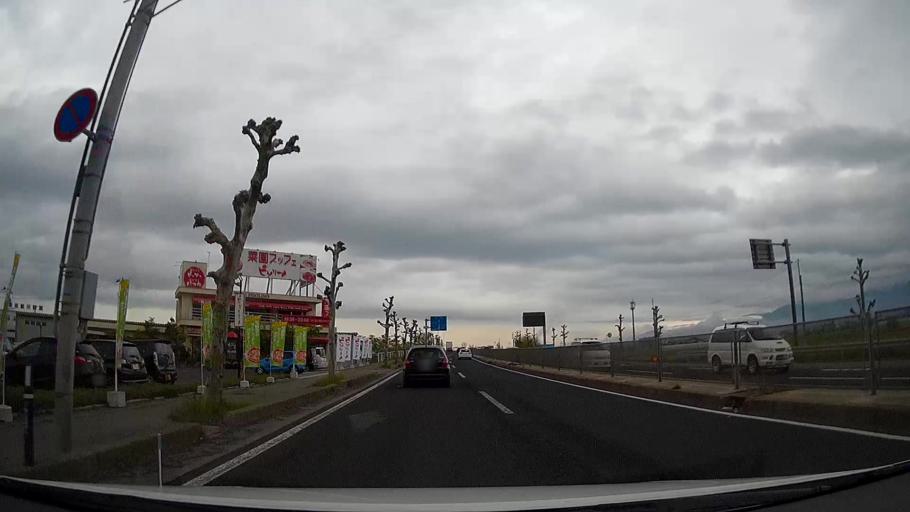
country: JP
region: Yamagata
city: Yamagata-shi
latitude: 38.2956
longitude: 140.3603
